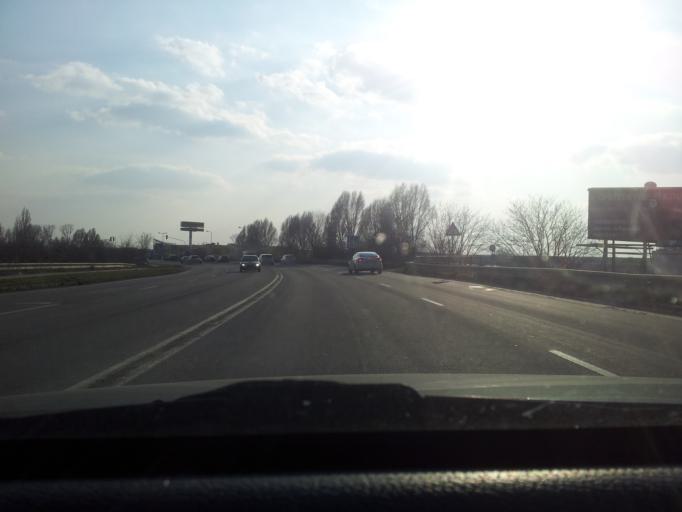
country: SK
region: Nitriansky
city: Levice
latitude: 48.2272
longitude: 18.6007
